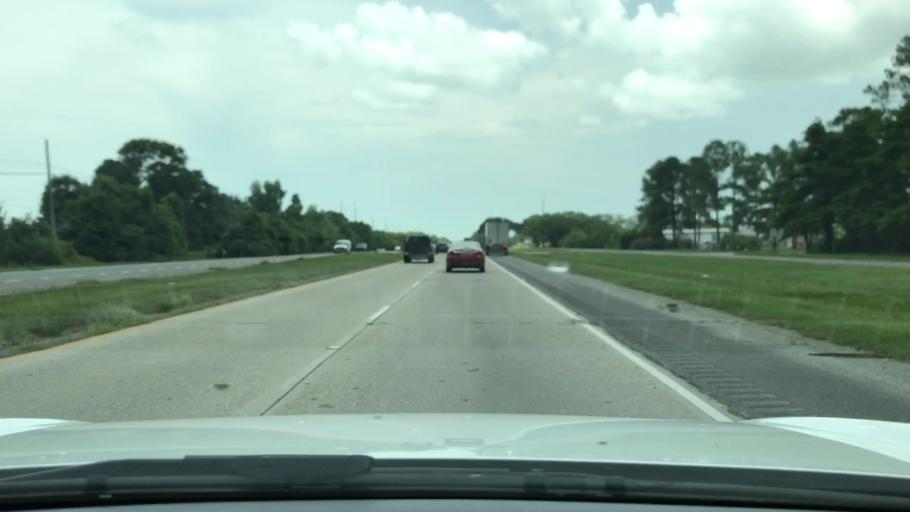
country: US
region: Louisiana
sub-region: Iberville Parish
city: Plaquemine
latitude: 30.3188
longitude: -91.2508
